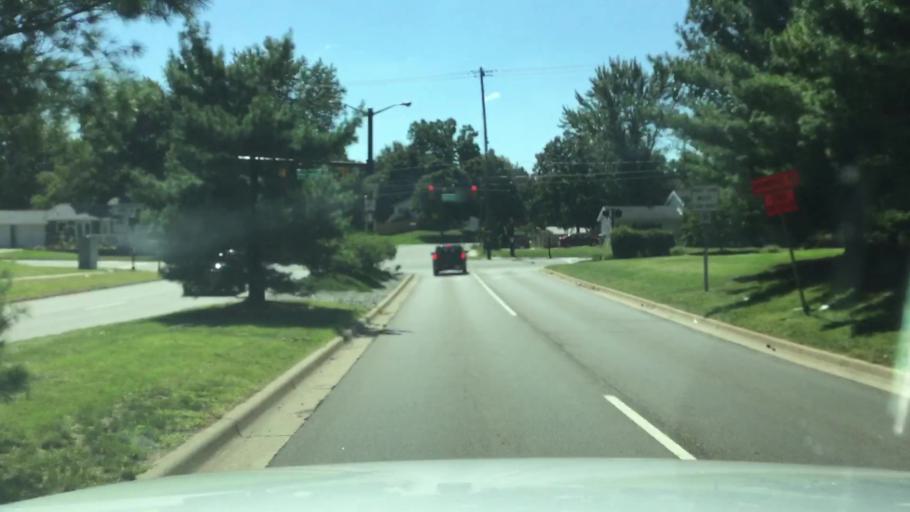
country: US
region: Michigan
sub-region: Kalamazoo County
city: Portage
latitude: 42.2162
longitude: -85.6032
